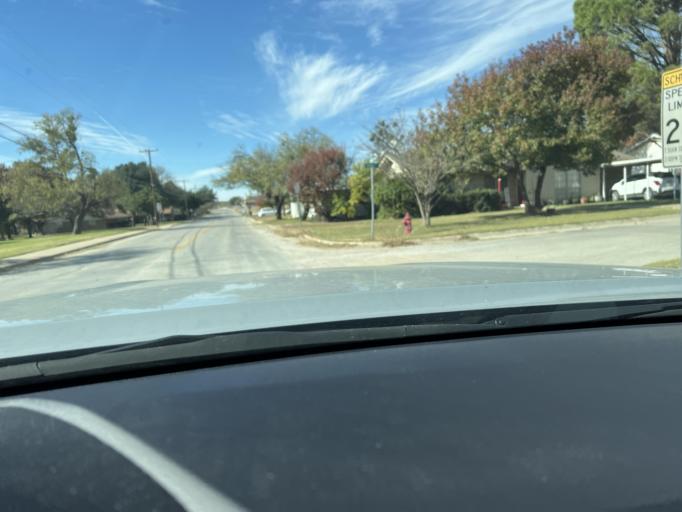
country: US
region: Texas
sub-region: Eastland County
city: Eastland
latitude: 32.3955
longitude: -98.8254
